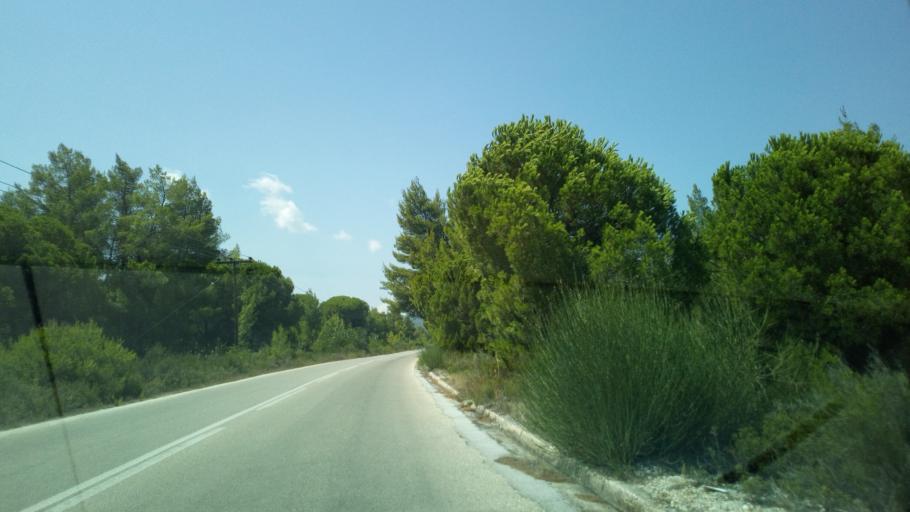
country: GR
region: Central Macedonia
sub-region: Nomos Chalkidikis
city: Sarti
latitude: 40.1246
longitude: 23.9532
